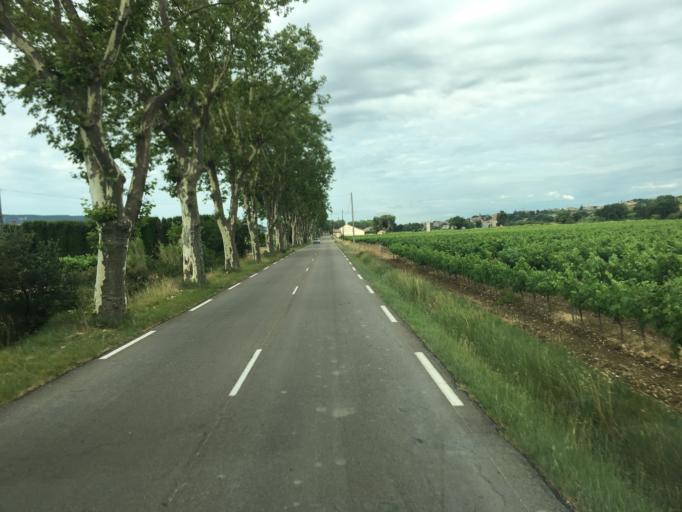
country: FR
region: Rhone-Alpes
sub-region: Departement de la Drome
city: Vinsobres
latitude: 44.3035
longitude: 5.0239
